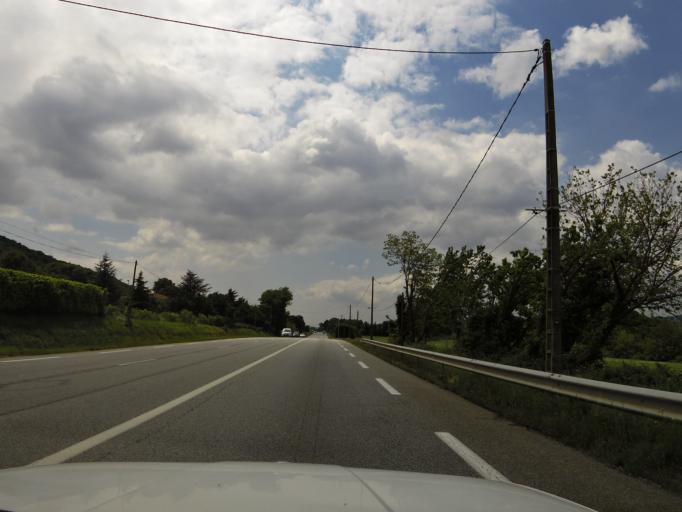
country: FR
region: Rhone-Alpes
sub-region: Departement de la Drome
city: Savasse
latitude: 44.6162
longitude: 4.7576
